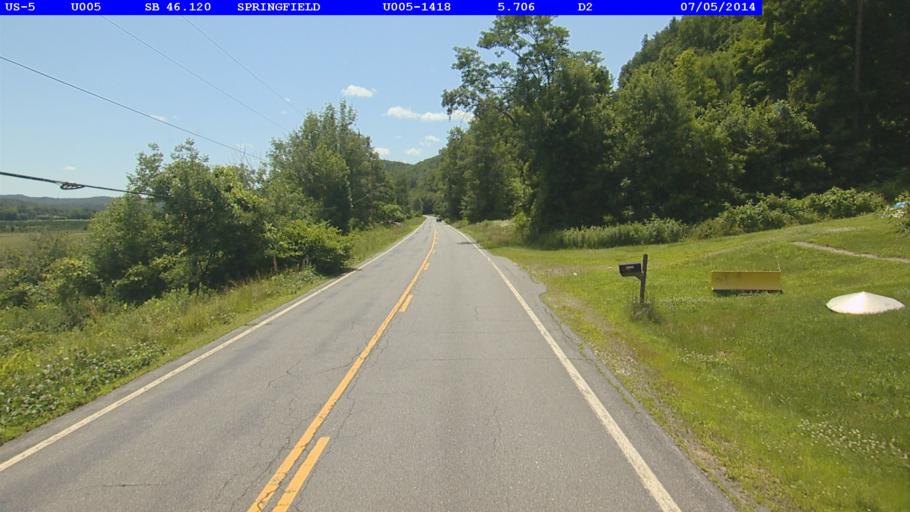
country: US
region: New Hampshire
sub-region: Sullivan County
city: Charlestown
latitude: 43.2953
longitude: -72.4099
